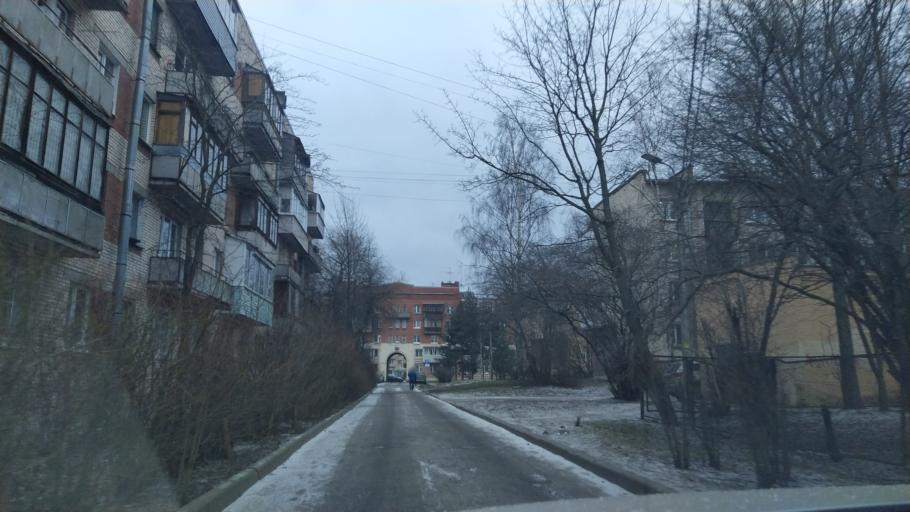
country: RU
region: St.-Petersburg
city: Pushkin
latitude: 59.7272
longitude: 30.4114
